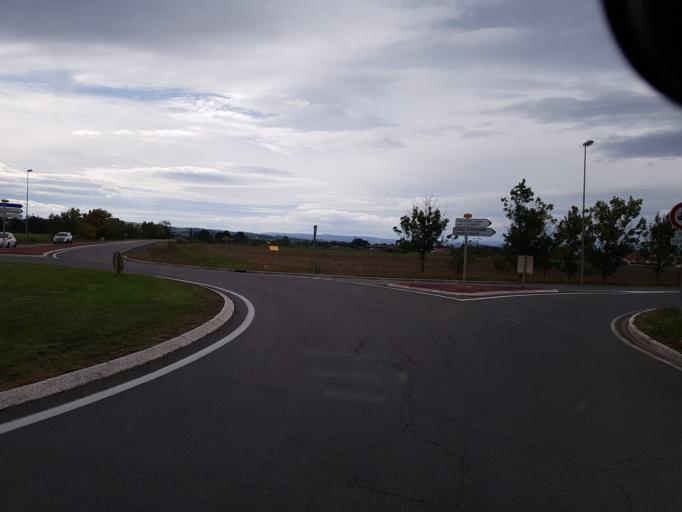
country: FR
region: Rhone-Alpes
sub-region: Departement de la Loire
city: Veauche
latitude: 45.5626
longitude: 4.3106
